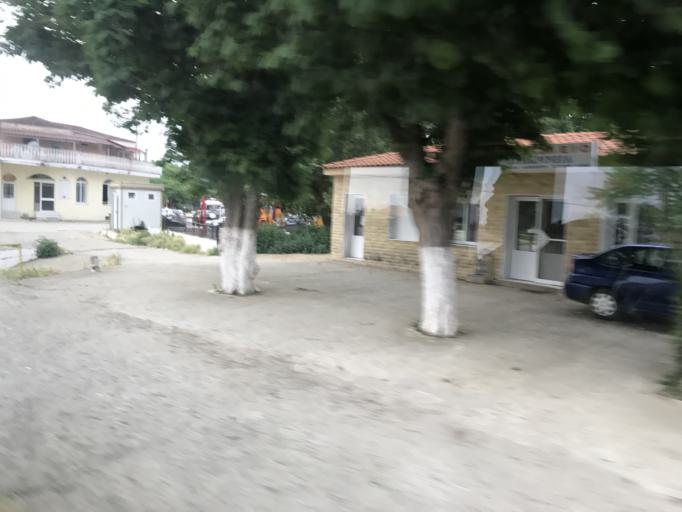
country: GR
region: East Macedonia and Thrace
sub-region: Nomos Rodopis
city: Aratos
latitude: 41.0807
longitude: 25.5542
